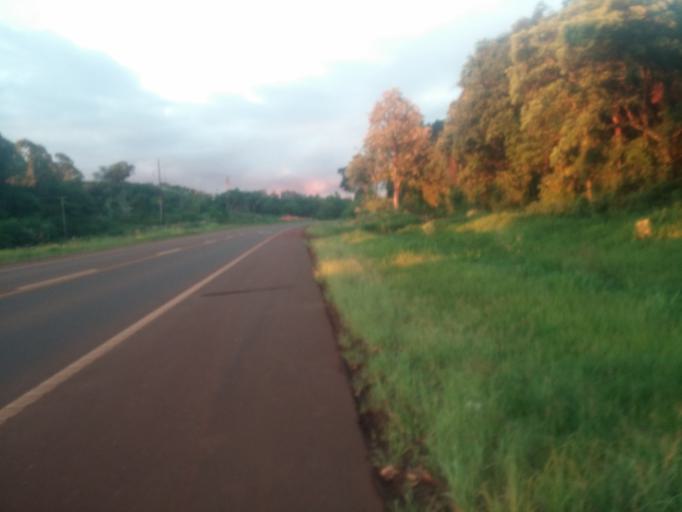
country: AR
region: Misiones
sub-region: Departamento de Obera
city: Obera
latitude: -27.4588
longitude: -55.0856
